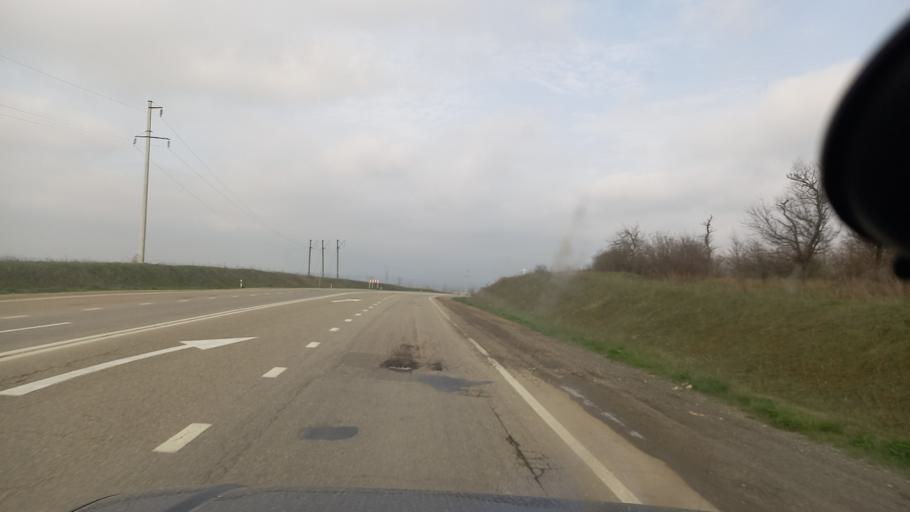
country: RU
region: Krasnodarskiy
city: Varenikovskaya
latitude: 45.1050
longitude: 37.6107
